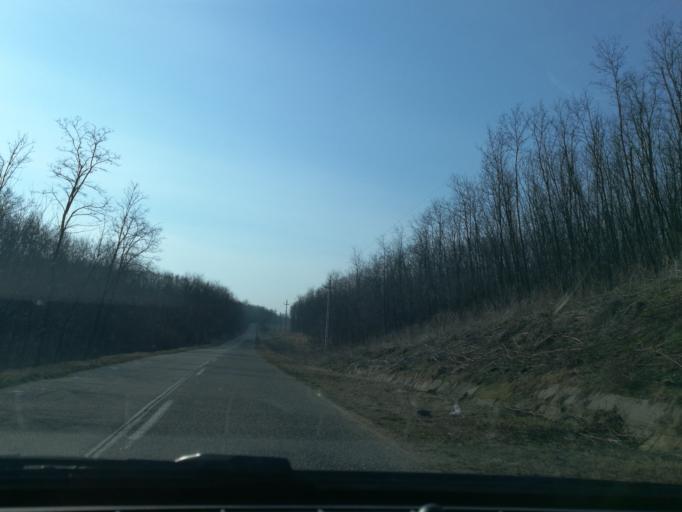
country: HU
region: Szabolcs-Szatmar-Bereg
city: Levelek
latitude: 47.9964
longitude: 21.9666
